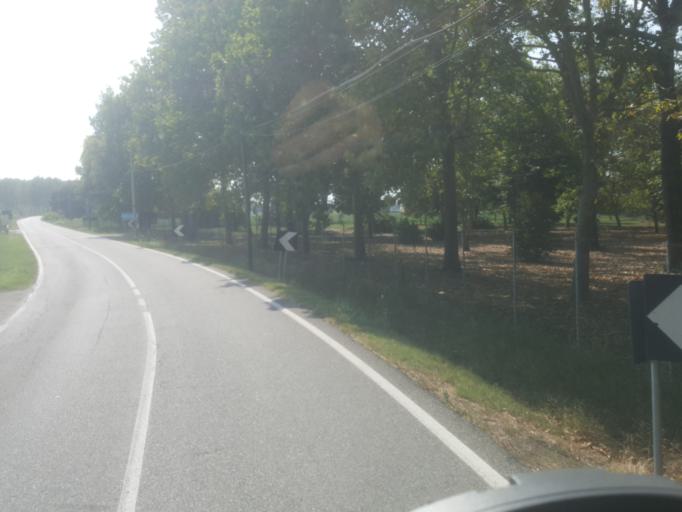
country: IT
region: Emilia-Romagna
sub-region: Provincia di Parma
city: Colorno
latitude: 44.9316
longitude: 10.3503
